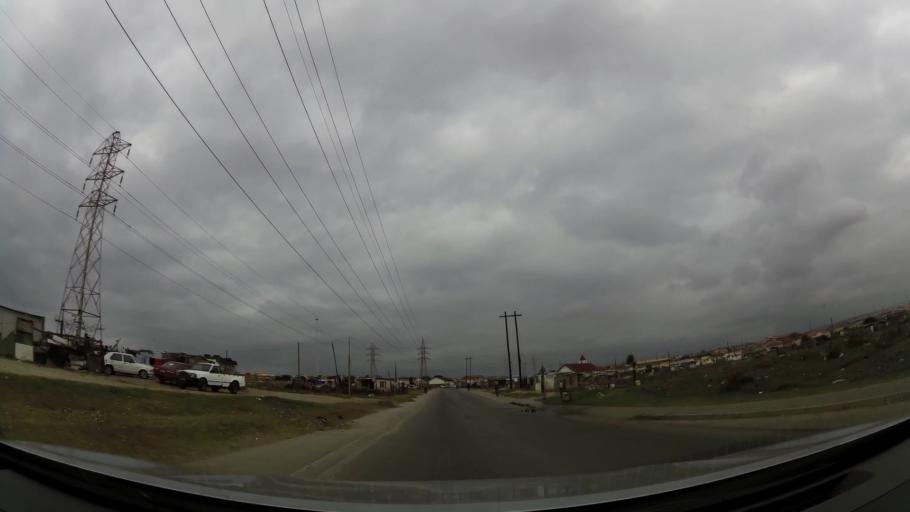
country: ZA
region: Eastern Cape
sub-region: Nelson Mandela Bay Metropolitan Municipality
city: Port Elizabeth
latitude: -33.8821
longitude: 25.5841
